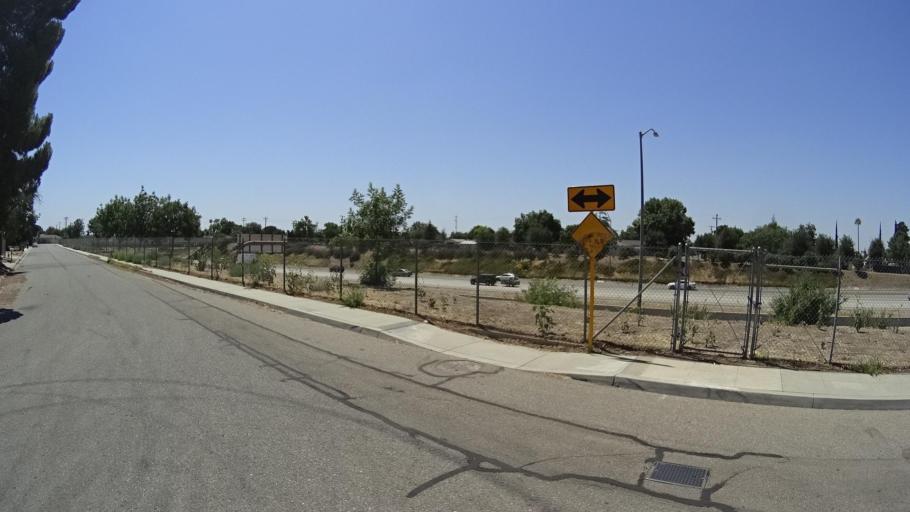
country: US
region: California
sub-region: Fresno County
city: Sunnyside
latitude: 36.7542
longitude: -119.7296
